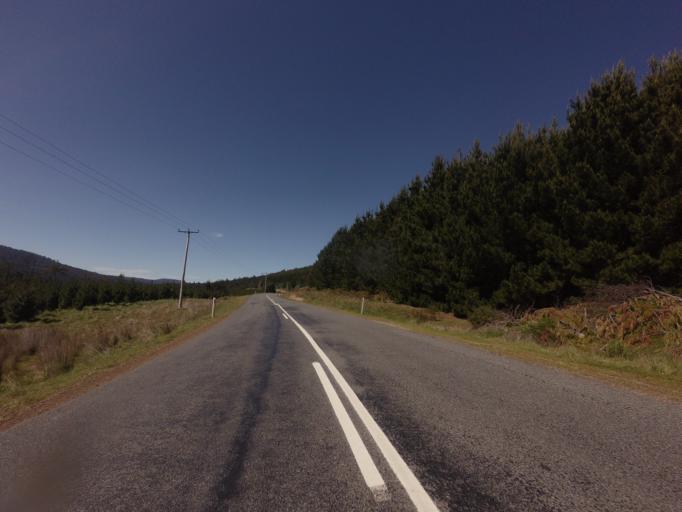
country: AU
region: Tasmania
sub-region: Derwent Valley
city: New Norfolk
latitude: -42.7468
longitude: 146.6507
